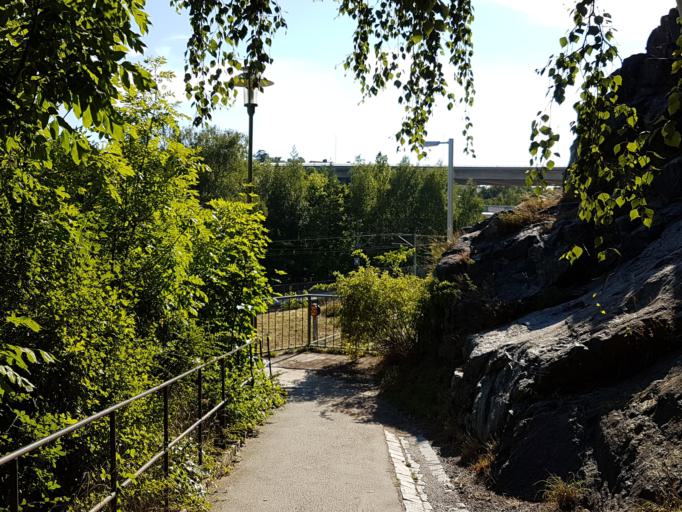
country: SE
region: Stockholm
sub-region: Solna Kommun
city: Solna
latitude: 59.3157
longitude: 18.0070
